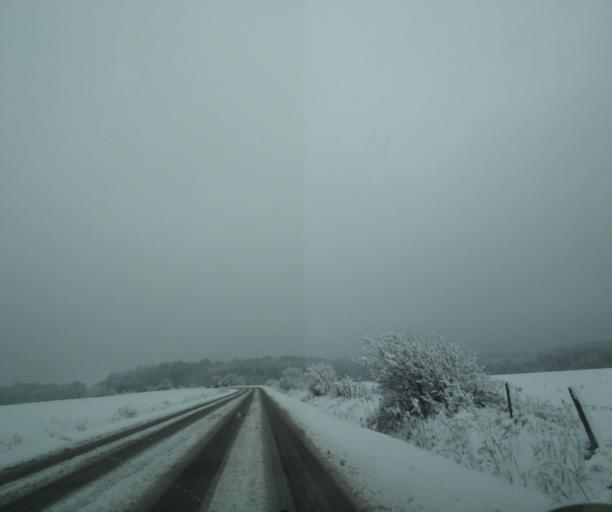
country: FR
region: Champagne-Ardenne
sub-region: Departement de la Haute-Marne
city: Saint-Dizier
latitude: 48.5973
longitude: 4.9081
